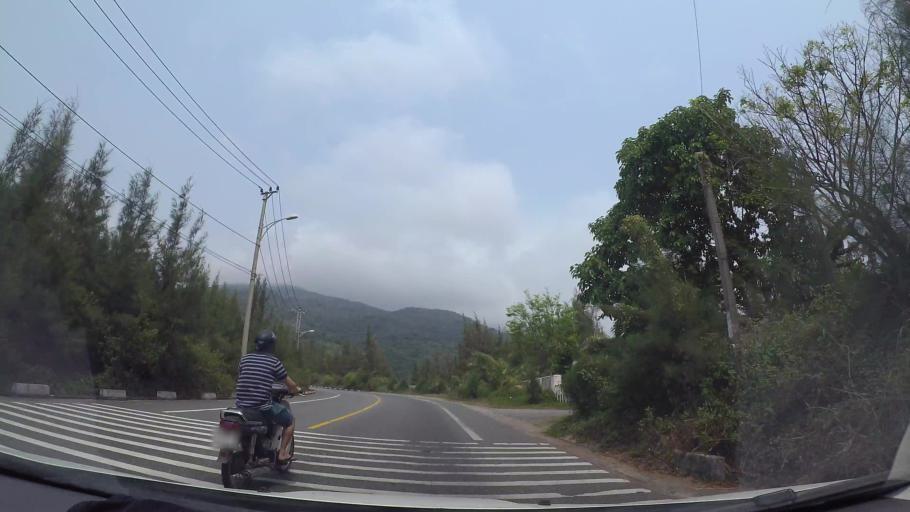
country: VN
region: Da Nang
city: Son Tra
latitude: 16.0977
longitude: 108.2693
